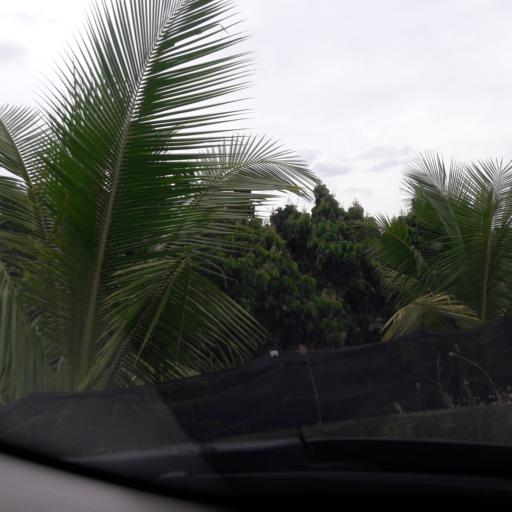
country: TH
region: Ratchaburi
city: Damnoen Saduak
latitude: 13.5750
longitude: 99.9445
